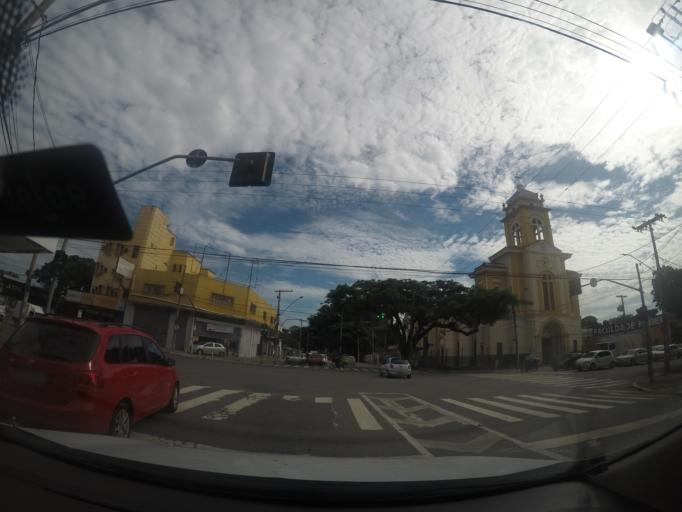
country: BR
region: Goias
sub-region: Goiania
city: Goiania
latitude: -16.6708
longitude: -49.2540
